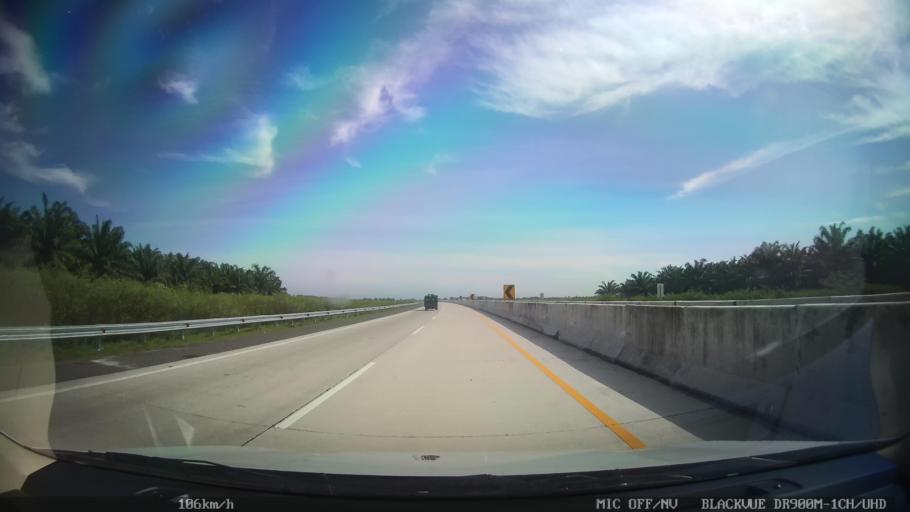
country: ID
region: North Sumatra
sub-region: Kabupaten Langkat
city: Stabat
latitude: 3.6908
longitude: 98.5399
